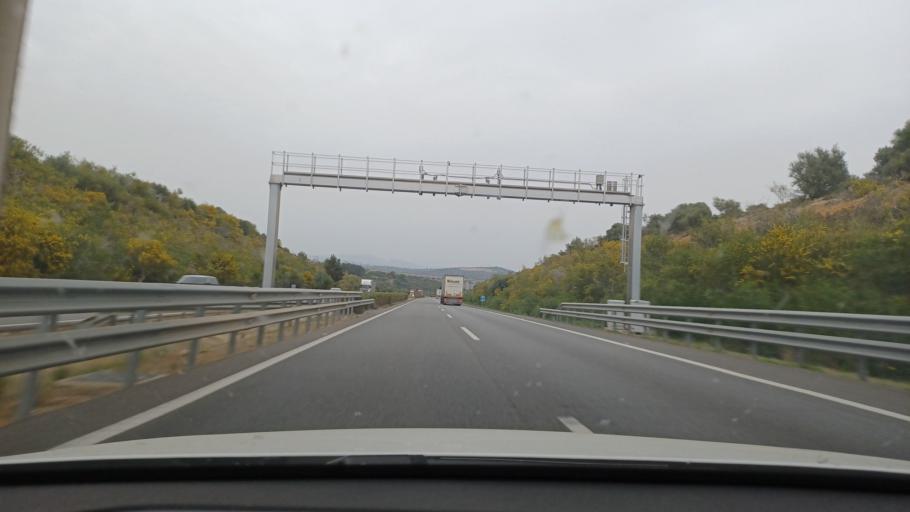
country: ES
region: Catalonia
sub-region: Provincia de Tarragona
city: Amposta
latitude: 40.7178
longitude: 0.5609
